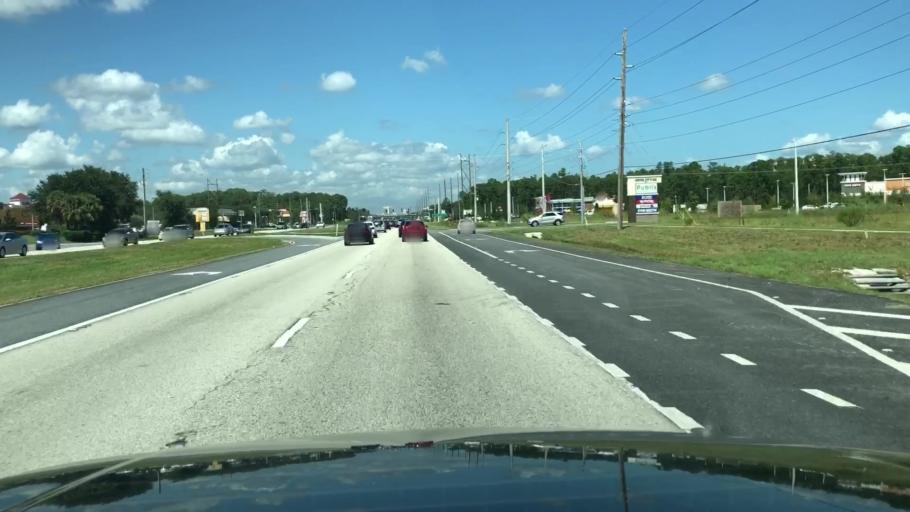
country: US
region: Florida
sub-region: Osceola County
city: Celebration
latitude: 28.3437
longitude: -81.4846
